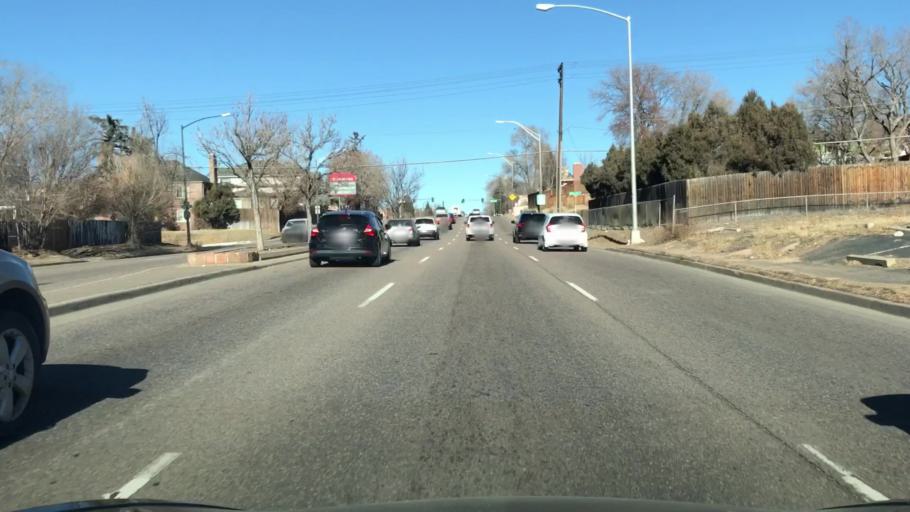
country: US
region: Colorado
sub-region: Arapahoe County
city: Glendale
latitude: 39.7155
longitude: -104.9406
